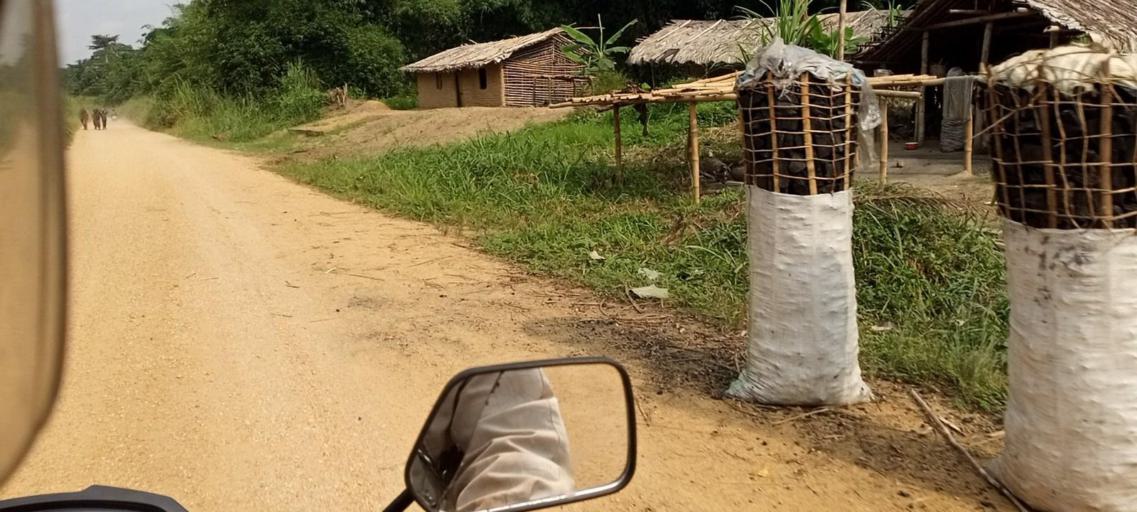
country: CD
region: Eastern Province
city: Kisangani
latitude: 0.3129
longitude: 25.4464
